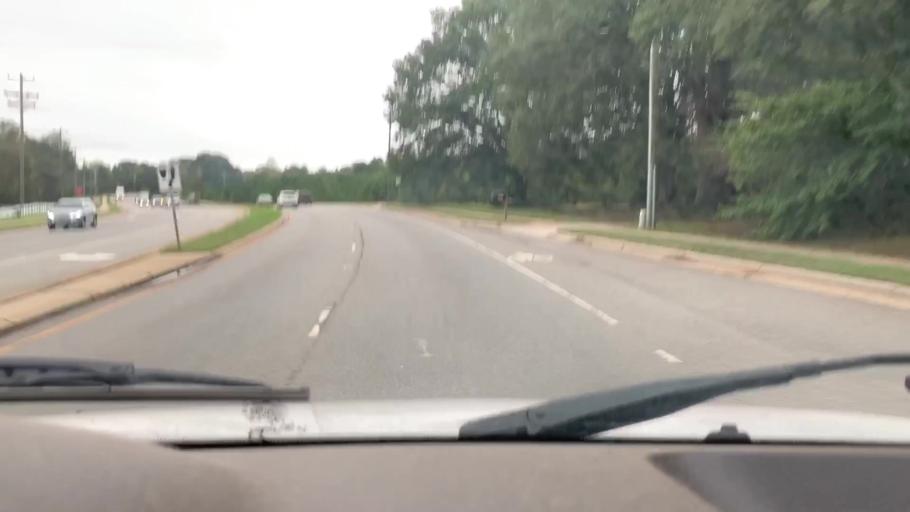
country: US
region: North Carolina
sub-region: Catawba County
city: Lake Norman of Catawba
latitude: 35.5692
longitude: -80.8980
